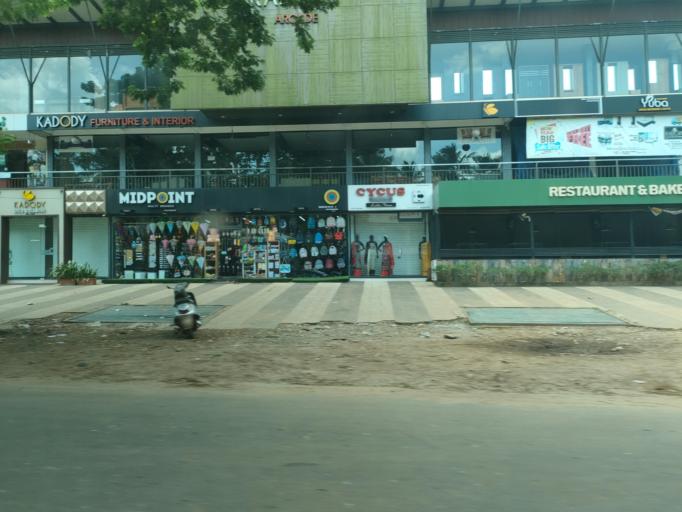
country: IN
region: Kerala
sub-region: Kozhikode
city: Mavoor
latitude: 11.2634
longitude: 75.8967
